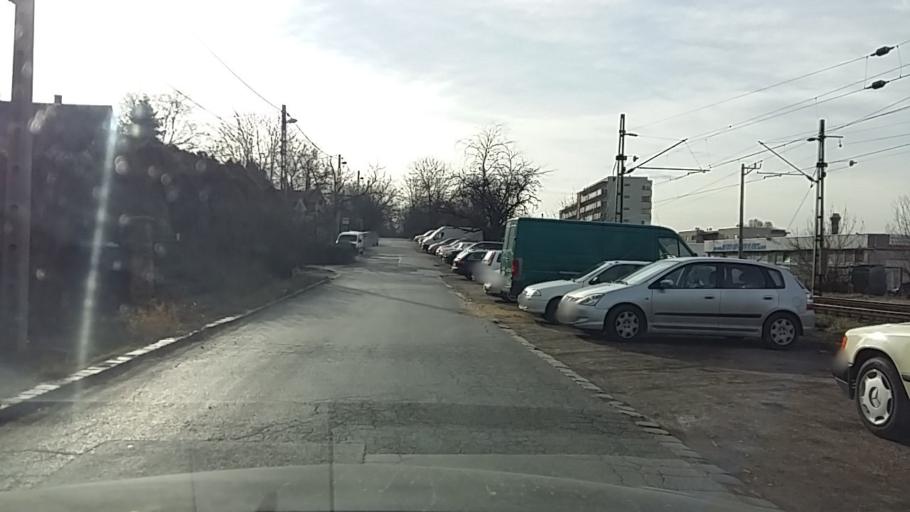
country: HU
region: Budapest
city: Budapest XVI. keruelet
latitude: 47.5140
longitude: 19.1525
